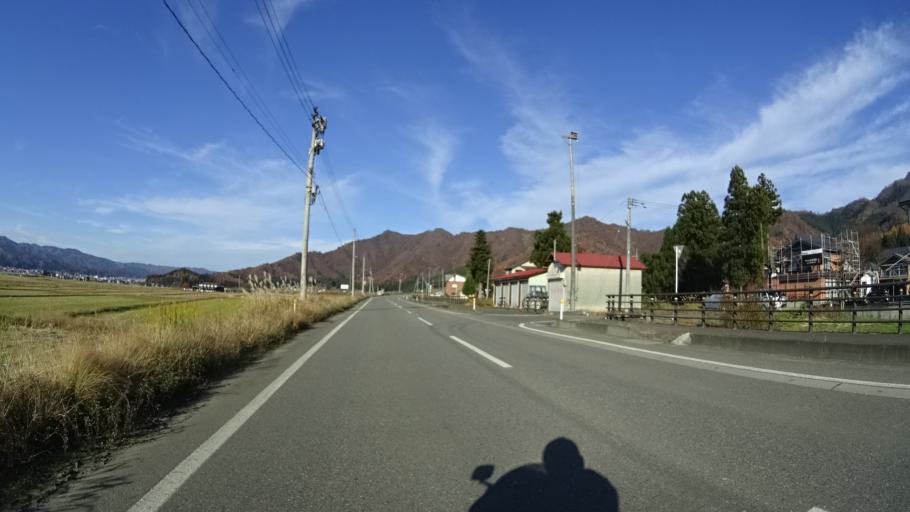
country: JP
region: Niigata
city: Muikamachi
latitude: 37.0331
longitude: 138.8875
